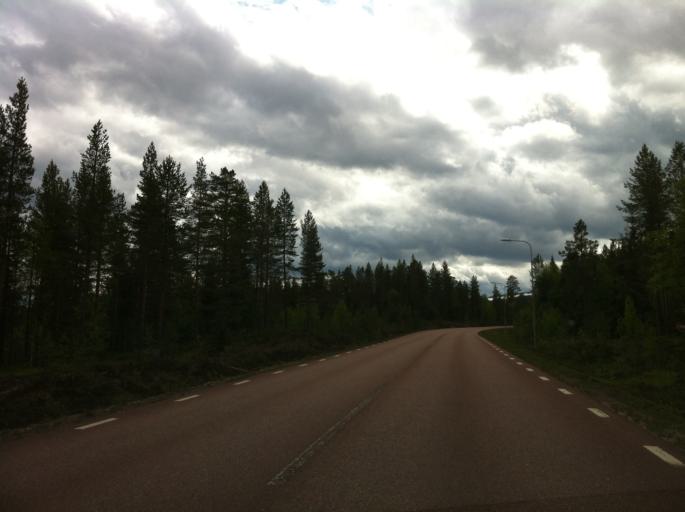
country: SE
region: Dalarna
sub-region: Malung-Saelens kommun
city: Malung
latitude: 61.1607
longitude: 13.2636
